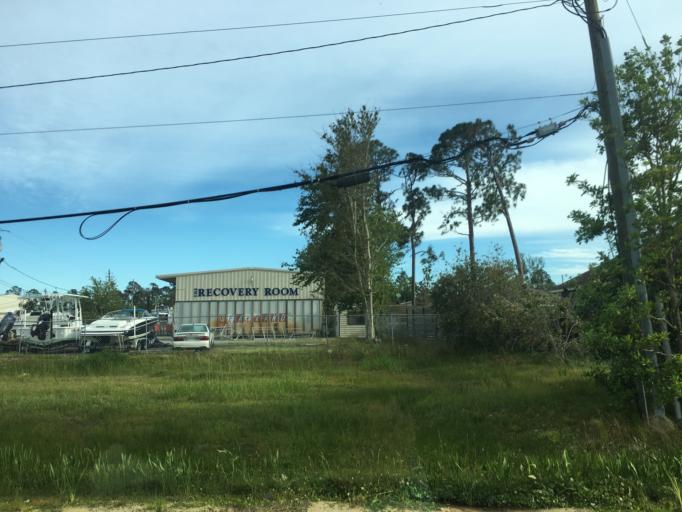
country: US
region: Florida
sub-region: Bay County
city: Upper Grand Lagoon
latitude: 30.1674
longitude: -85.7582
